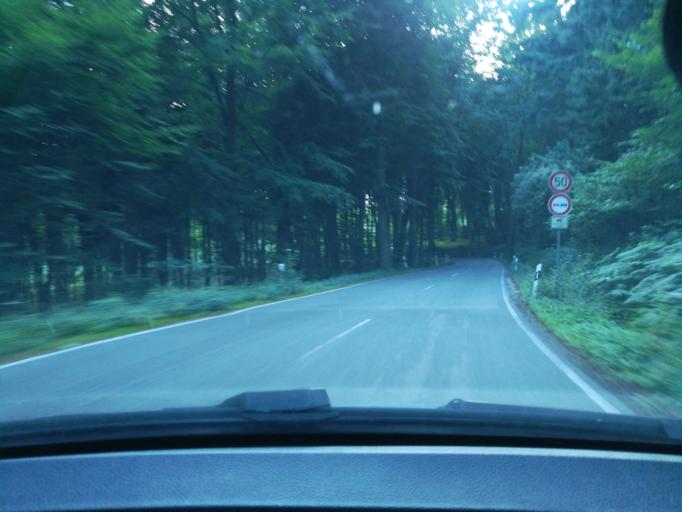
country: DE
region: North Rhine-Westphalia
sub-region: Regierungsbezirk Munster
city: Lienen
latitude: 52.1614
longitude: 7.9733
